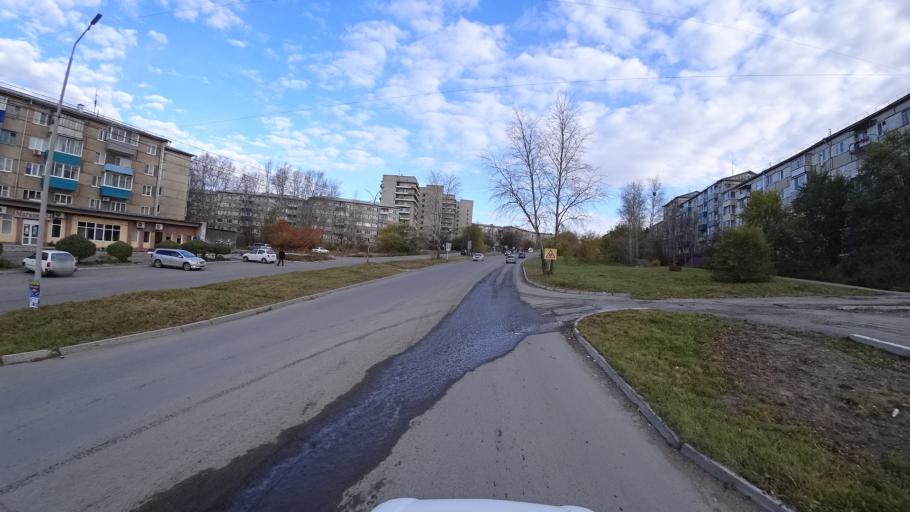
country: RU
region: Khabarovsk Krai
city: Amursk
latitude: 50.2378
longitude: 136.9111
